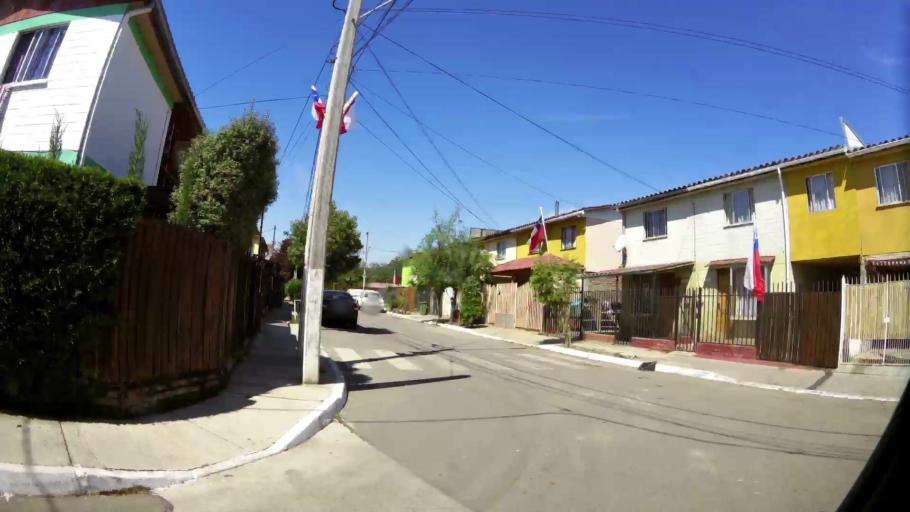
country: CL
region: Santiago Metropolitan
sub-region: Provincia de Talagante
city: Penaflor
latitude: -33.6136
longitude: -70.8996
